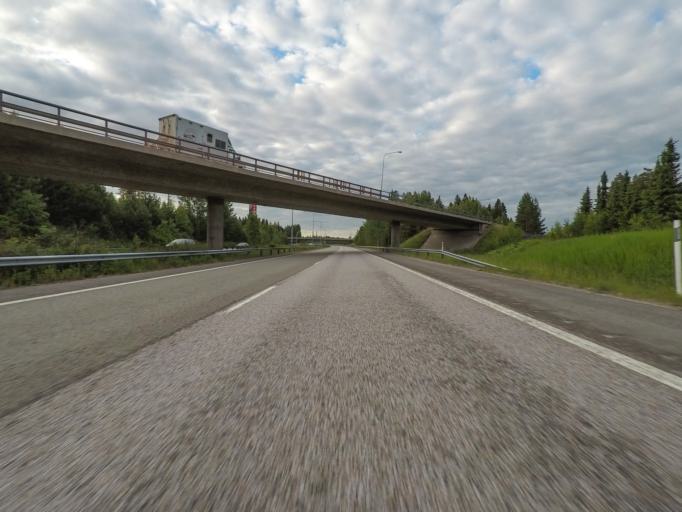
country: FI
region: Paijanne Tavastia
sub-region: Lahti
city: Heinola
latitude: 61.1902
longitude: 26.0015
